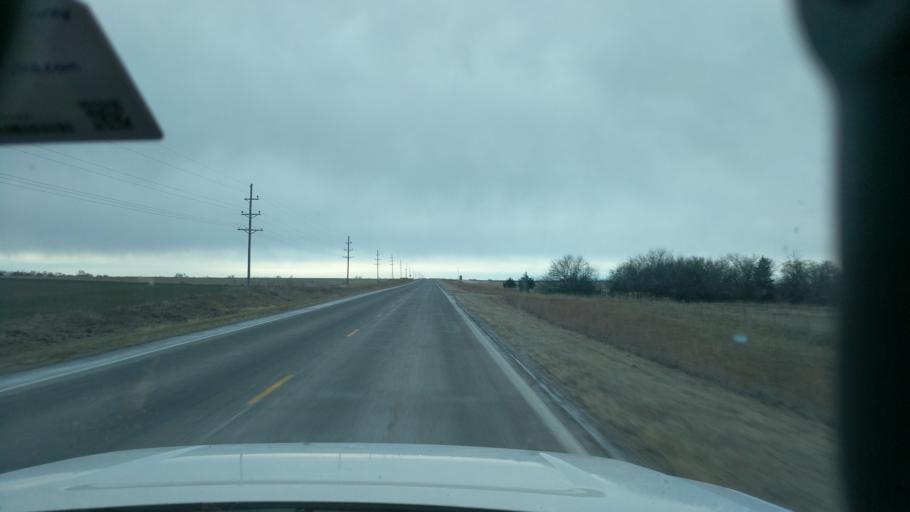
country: US
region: Kansas
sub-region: Marion County
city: Hillsboro
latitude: 38.3164
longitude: -97.3348
